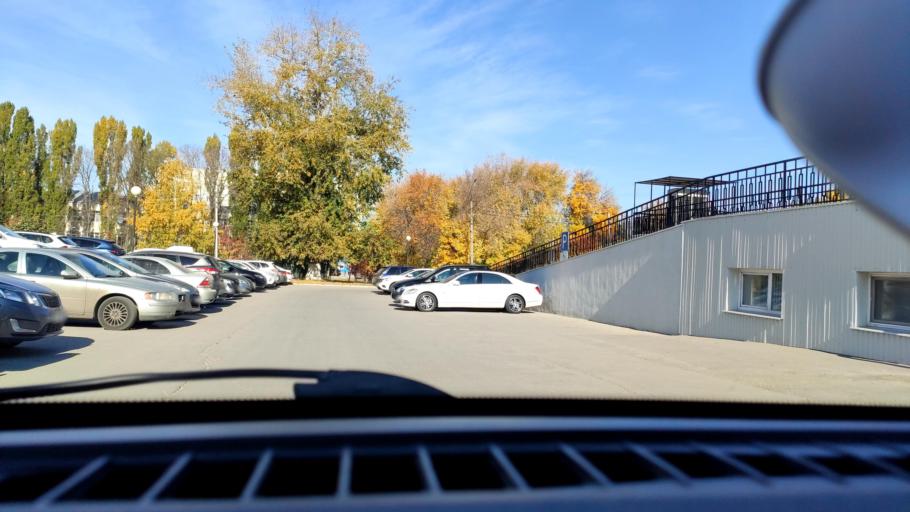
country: RU
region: Samara
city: Samara
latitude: 53.2029
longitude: 50.1695
